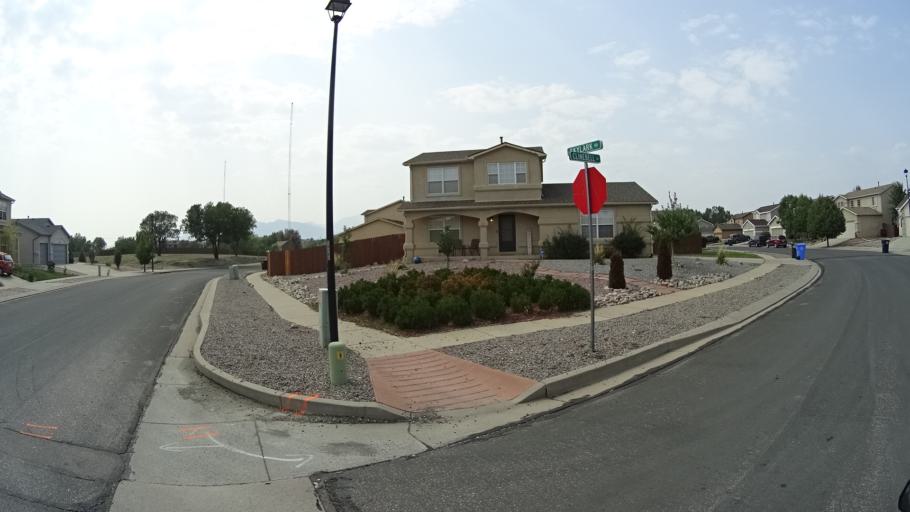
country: US
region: Colorado
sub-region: El Paso County
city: Cimarron Hills
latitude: 38.8272
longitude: -104.7403
